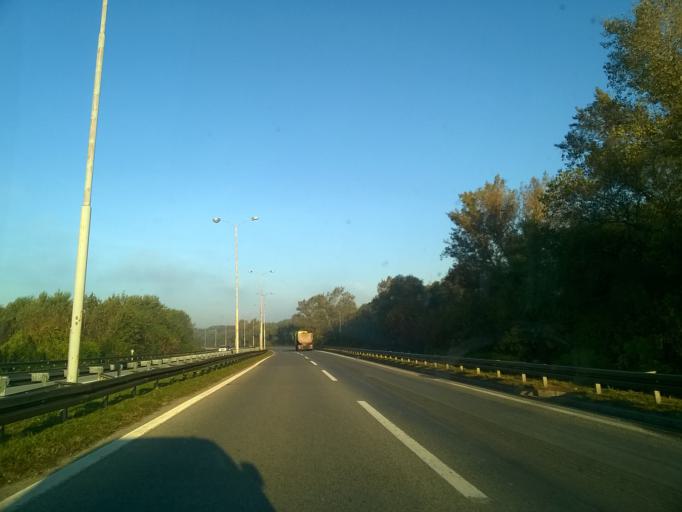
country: RS
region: Autonomna Pokrajina Vojvodina
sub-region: Juznobanatski Okrug
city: Pancevo
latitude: 44.8558
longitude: 20.6275
